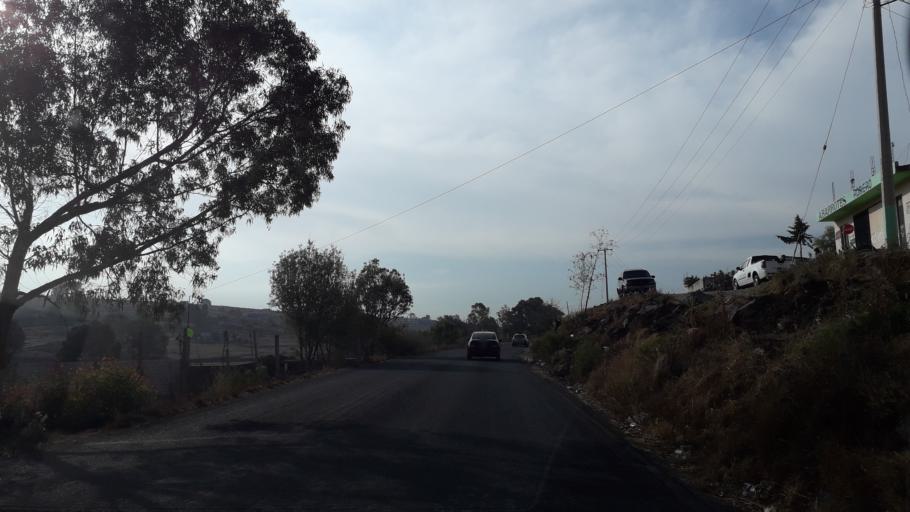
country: MX
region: Puebla
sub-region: Puebla
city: San Andres Azumiatla
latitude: 18.9195
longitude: -98.2490
